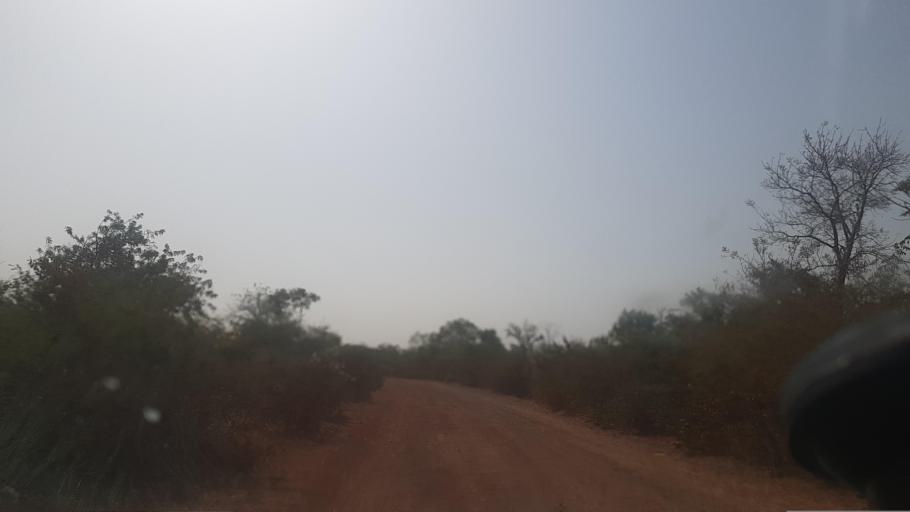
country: ML
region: Segou
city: Baroueli
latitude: 13.0695
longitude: -6.4797
